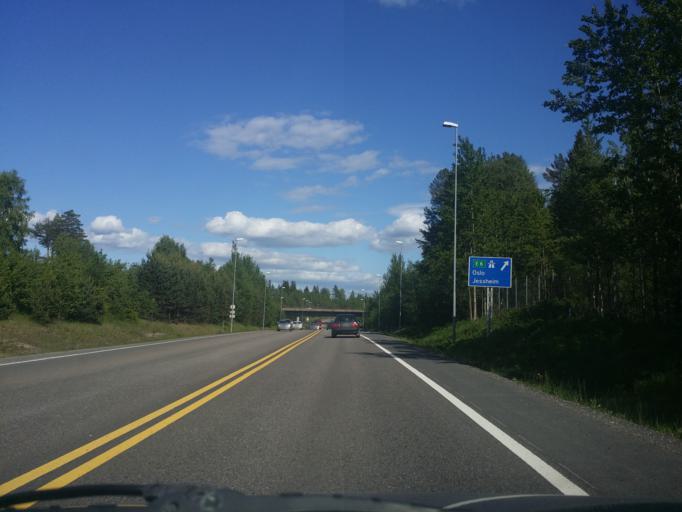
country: NO
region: Akershus
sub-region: Nannestad
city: Teigebyen
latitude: 60.1780
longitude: 11.0885
